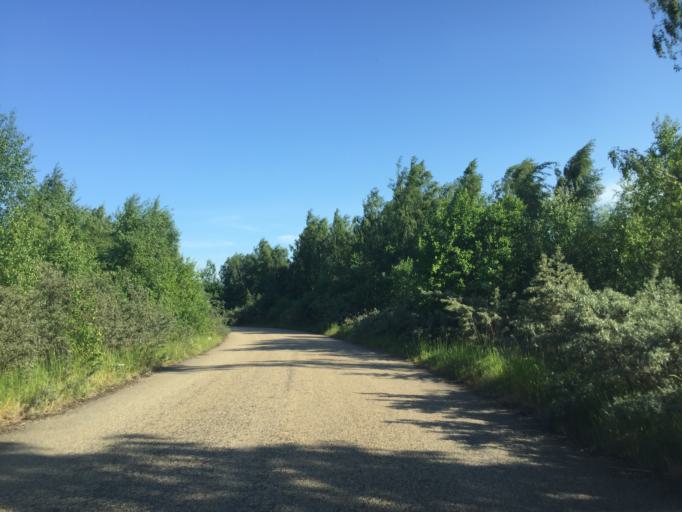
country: DK
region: Capital Region
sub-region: Kobenhavn
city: Copenhagen
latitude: 55.6313
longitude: 12.5484
